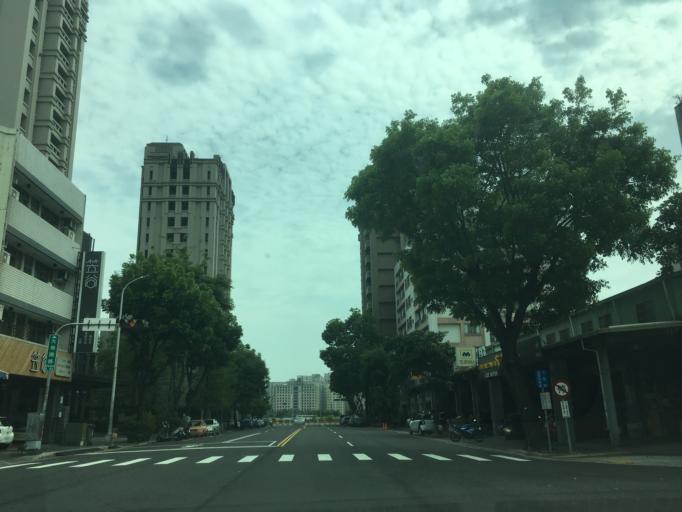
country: TW
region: Taiwan
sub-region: Taichung City
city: Taichung
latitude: 24.1308
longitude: 120.6499
